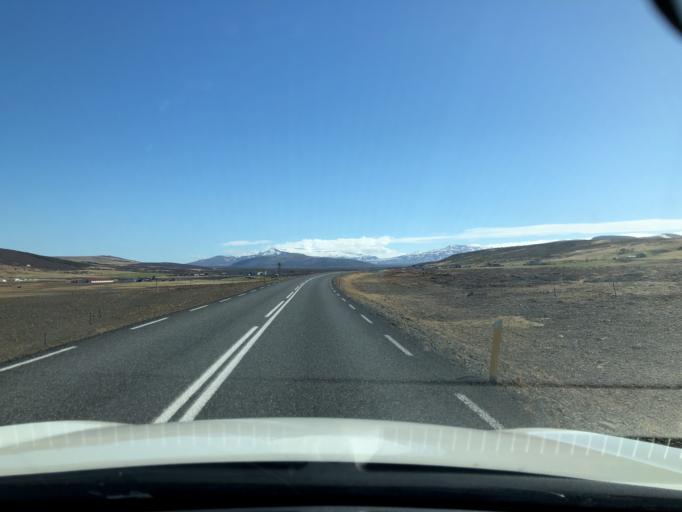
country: IS
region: South
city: Hveragerdi
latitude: 64.6995
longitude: -21.0580
